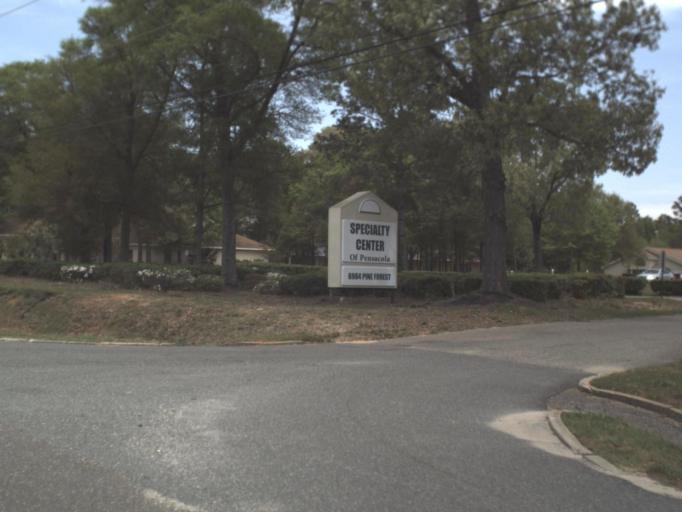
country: US
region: Florida
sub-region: Escambia County
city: Bellview
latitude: 30.4893
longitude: -87.3062
